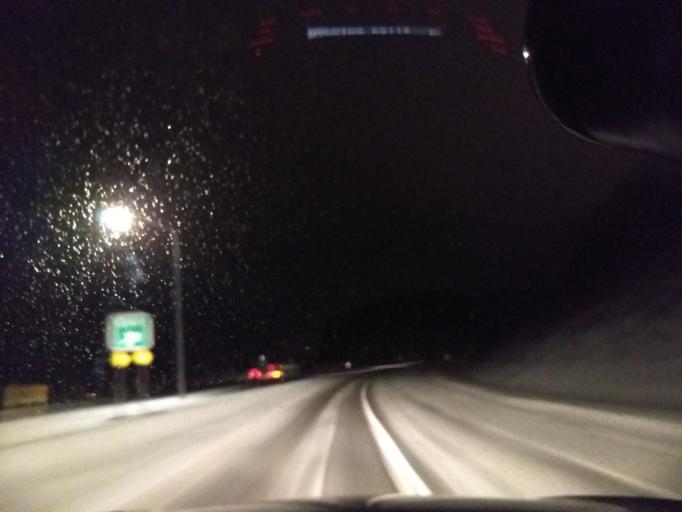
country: US
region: Pennsylvania
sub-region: Cambria County
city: Cresson
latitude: 40.4470
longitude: -78.5959
